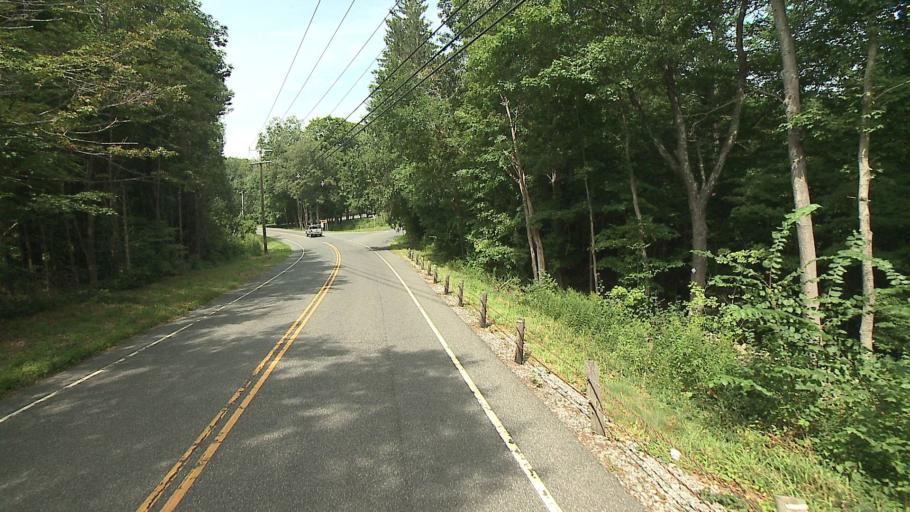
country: US
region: Connecticut
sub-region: Litchfield County
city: Woodbury
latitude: 41.5925
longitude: -73.2336
